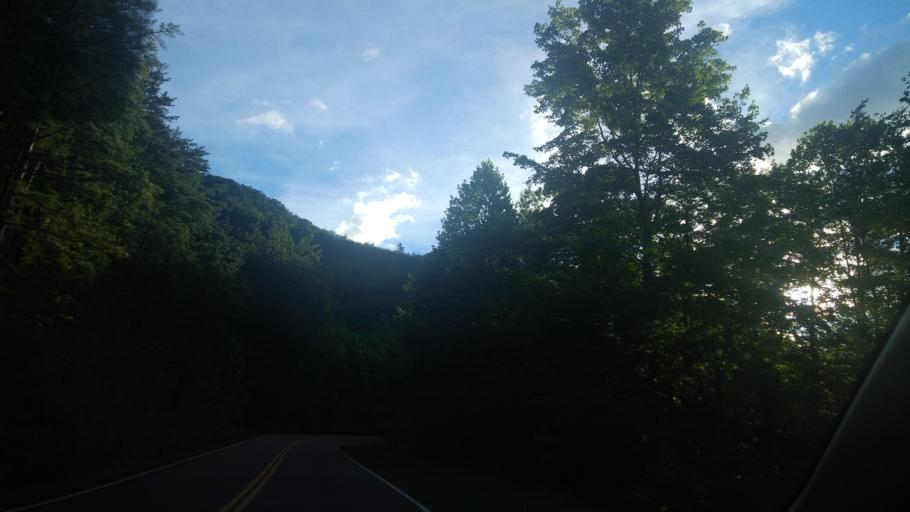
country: US
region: Tennessee
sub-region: Cocke County
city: Newport
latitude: 35.8074
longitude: -83.2347
